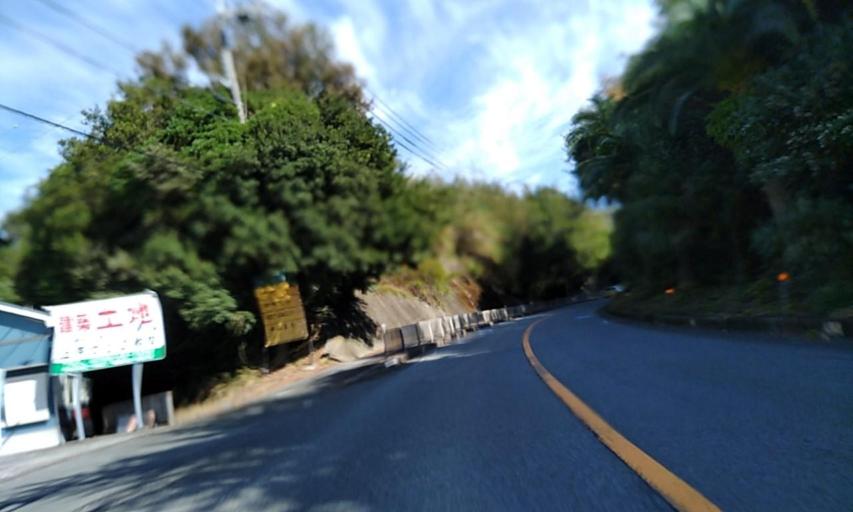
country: JP
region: Wakayama
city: Gobo
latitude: 33.8124
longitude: 135.2088
